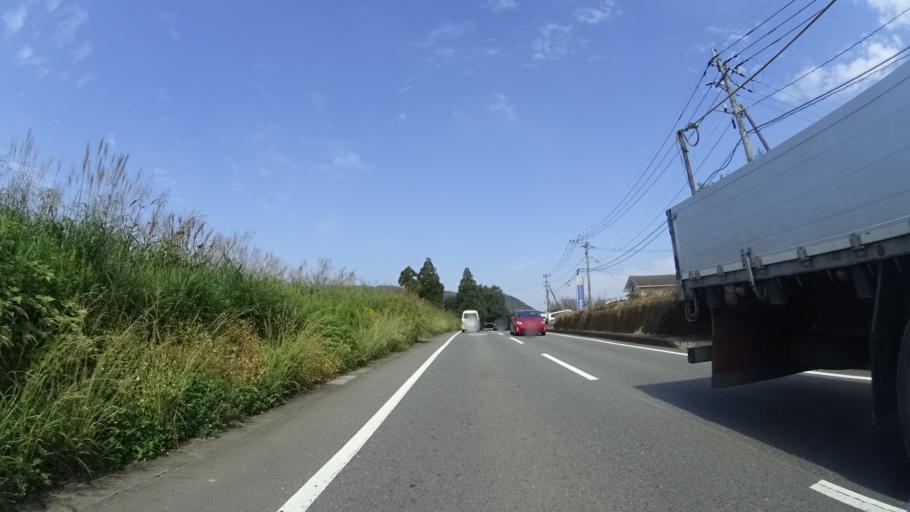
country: JP
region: Kumamoto
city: Matsubase
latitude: 32.6645
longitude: 130.7181
